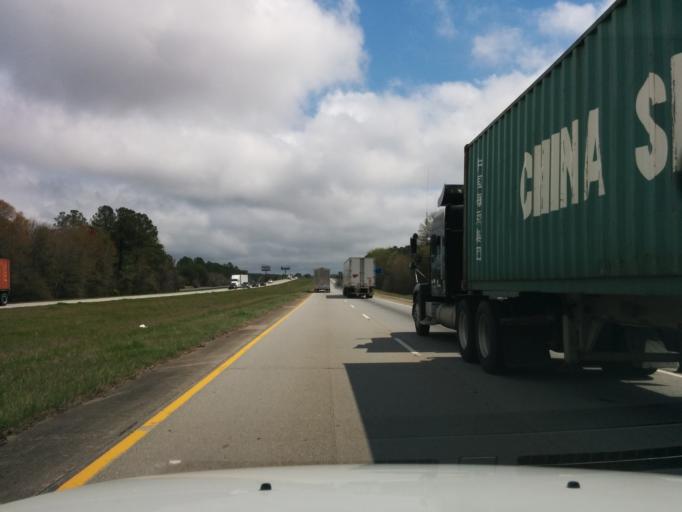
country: US
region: Georgia
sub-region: Emanuel County
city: Swainsboro
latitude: 32.4081
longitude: -82.3326
